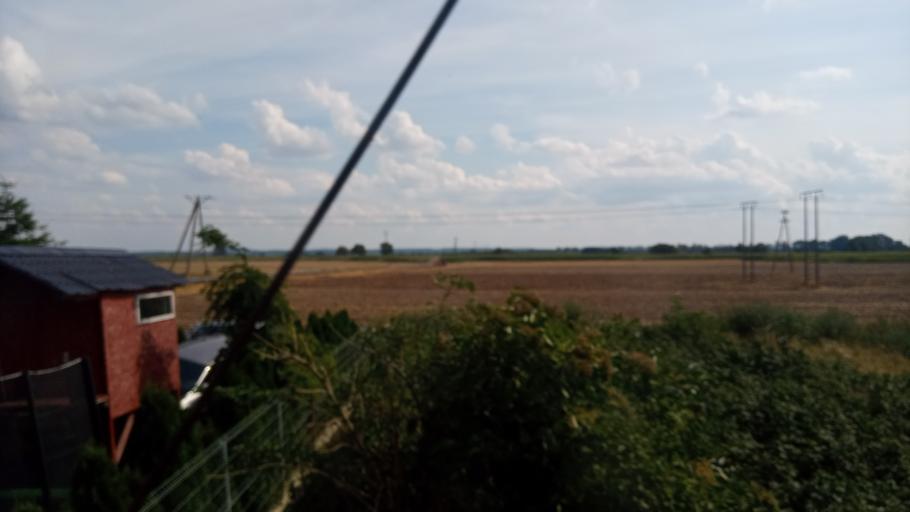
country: PL
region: Greater Poland Voivodeship
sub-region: Powiat pilski
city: Osiek nad Notecia
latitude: 53.1200
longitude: 17.3080
